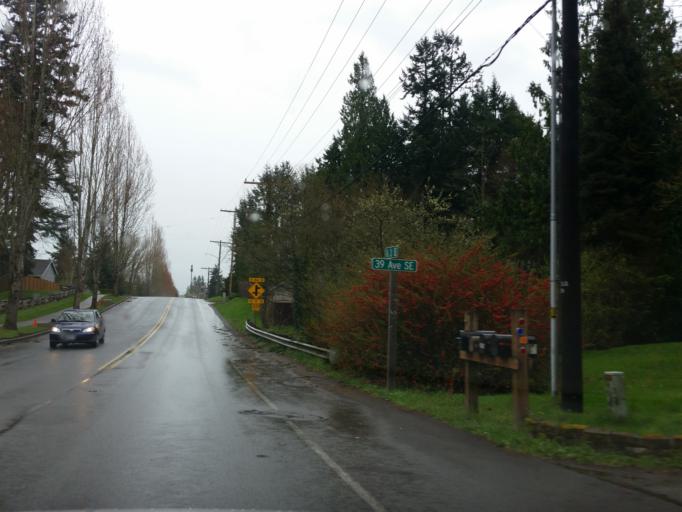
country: US
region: Washington
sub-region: Snohomish County
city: Silver Firs
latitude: 47.8924
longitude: -122.1801
